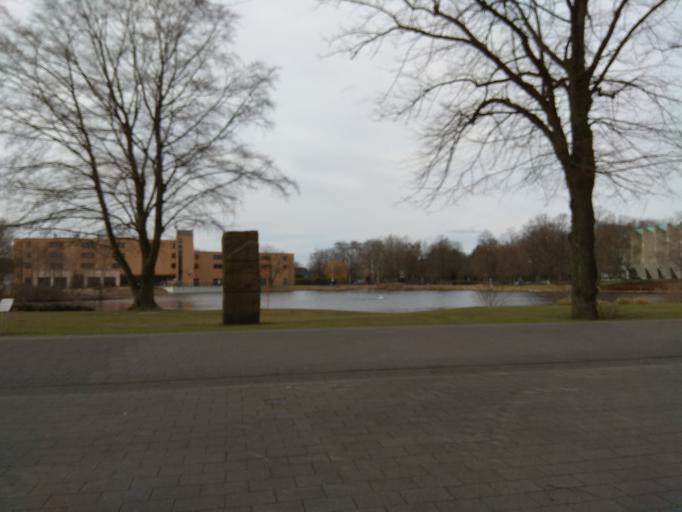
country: DE
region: North Rhine-Westphalia
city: Marl
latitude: 51.6546
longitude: 7.0938
